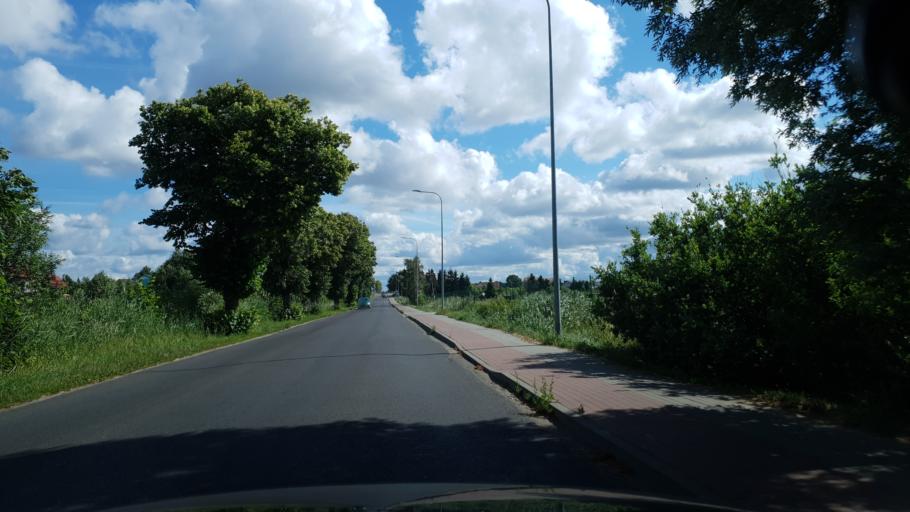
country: PL
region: Pomeranian Voivodeship
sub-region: Powiat pucki
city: Mosty
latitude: 54.6248
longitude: 18.4965
